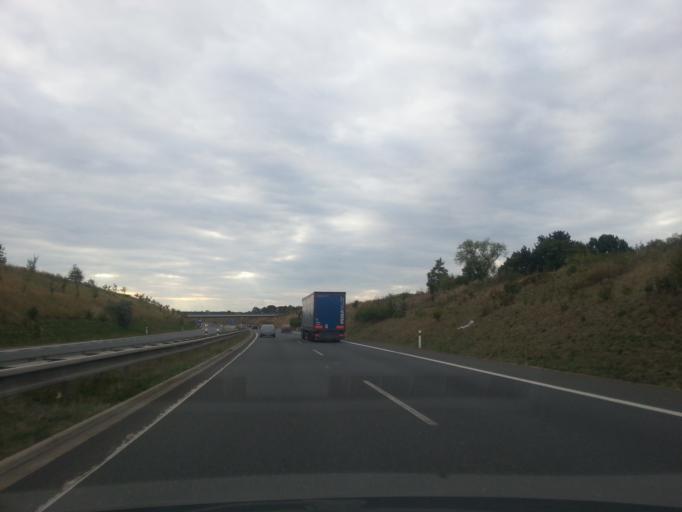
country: CZ
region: Central Bohemia
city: Jenec
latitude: 50.0972
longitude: 14.2157
